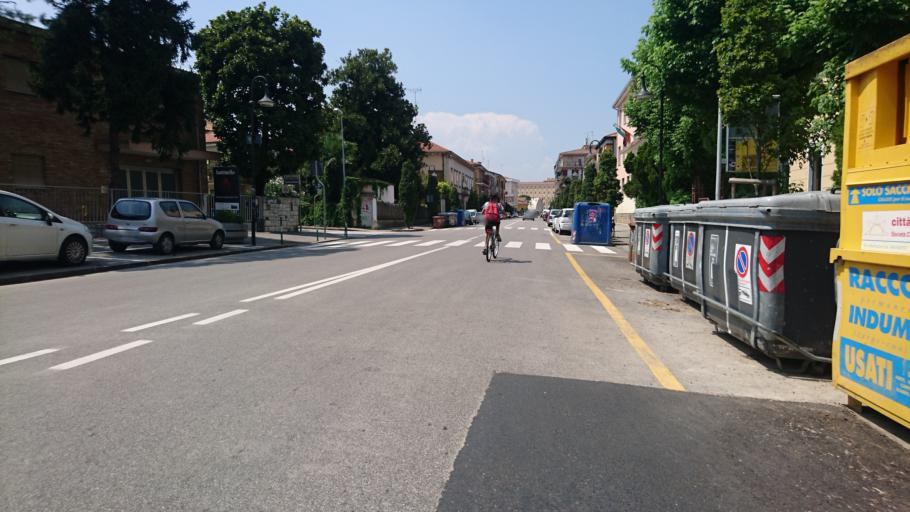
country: IT
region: Veneto
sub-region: Provincia di Padova
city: Padova
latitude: 45.4219
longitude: 11.8858
